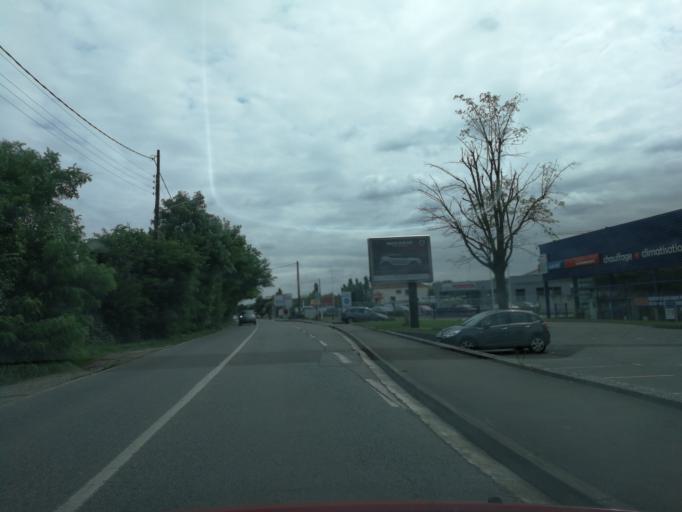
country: FR
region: Midi-Pyrenees
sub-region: Departement de la Haute-Garonne
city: Ramonville-Saint-Agne
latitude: 43.5702
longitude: 1.4986
